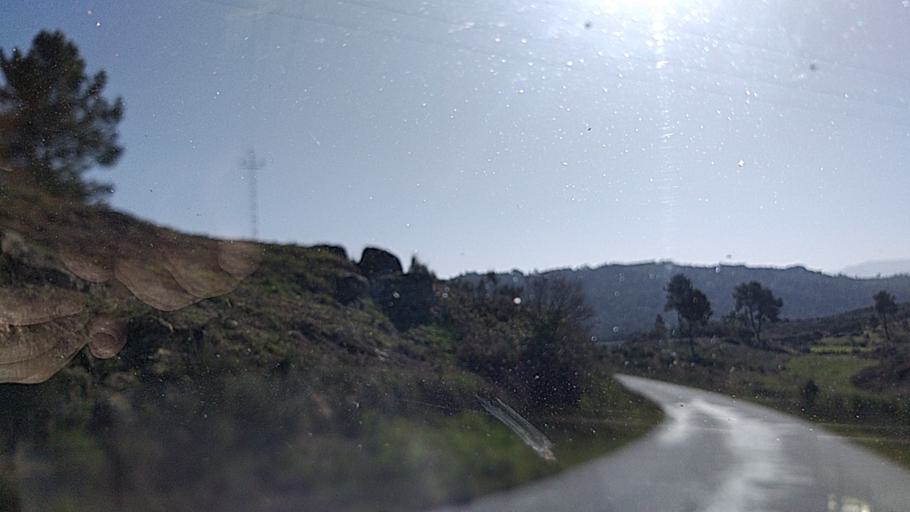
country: PT
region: Guarda
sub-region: Celorico da Beira
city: Celorico da Beira
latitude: 40.6859
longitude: -7.4158
